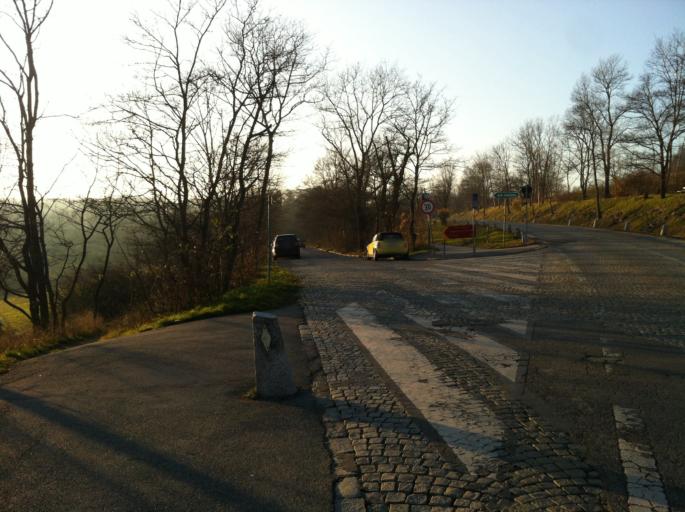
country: AT
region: Lower Austria
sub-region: Politischer Bezirk Wien-Umgebung
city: Klosterneuburg
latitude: 48.2634
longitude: 16.3193
